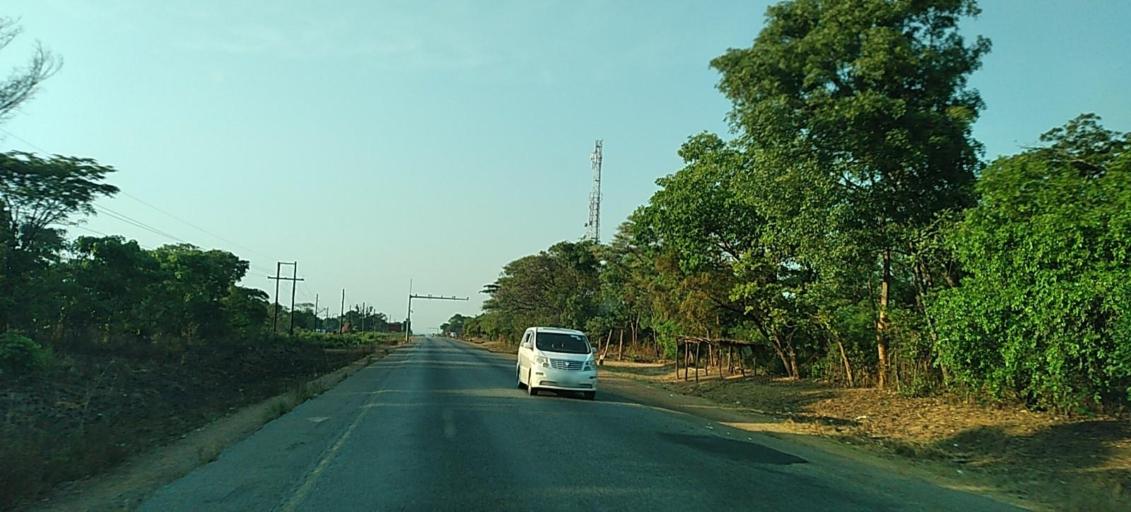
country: ZM
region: Copperbelt
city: Luanshya
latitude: -13.2414
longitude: 28.6784
